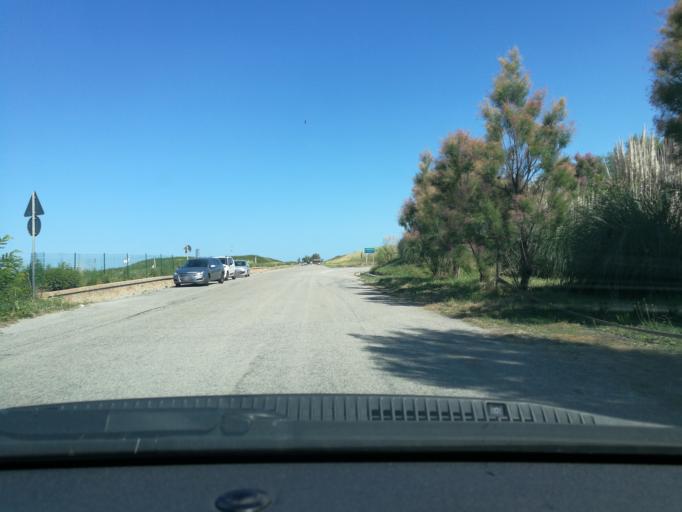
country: IT
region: Abruzzo
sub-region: Provincia di Chieti
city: Vasto
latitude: 42.1741
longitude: 14.6973
